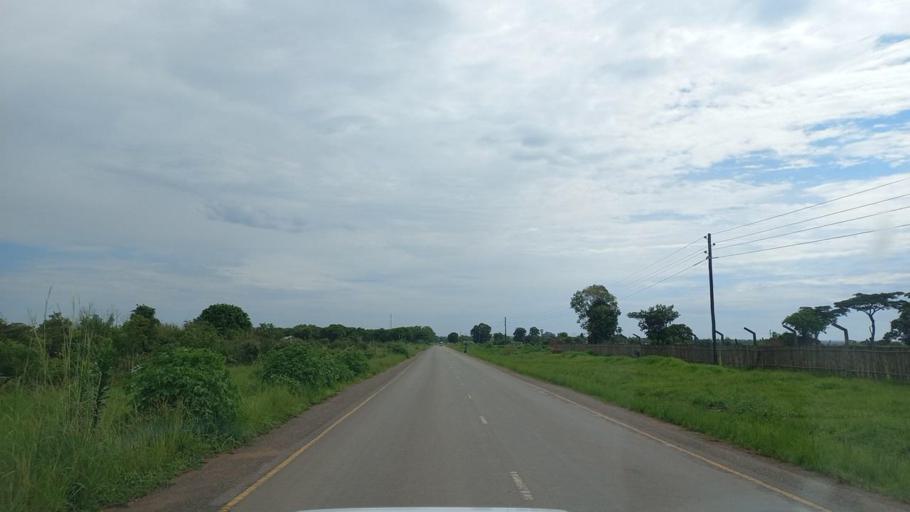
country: ZM
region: Copperbelt
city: Kitwe
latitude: -12.8819
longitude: 28.3198
